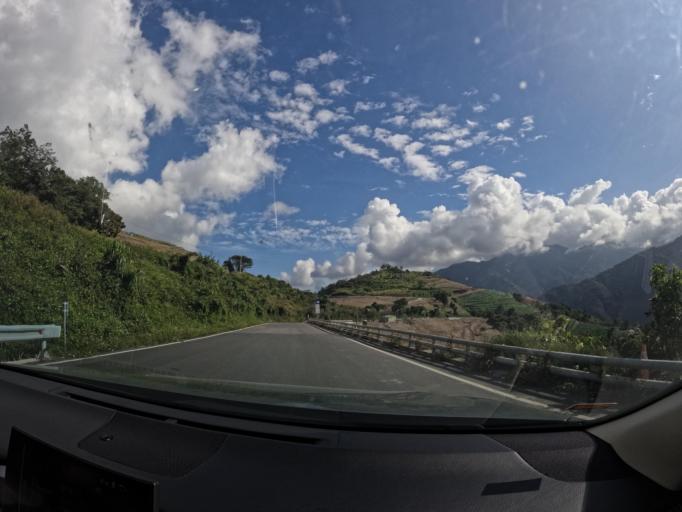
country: TW
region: Taiwan
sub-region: Taitung
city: Taitung
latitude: 23.1999
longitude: 121.0250
